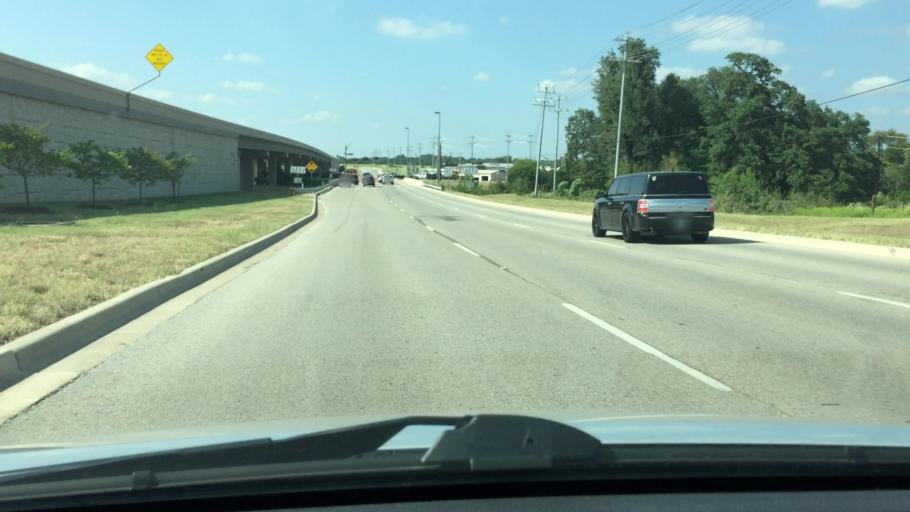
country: US
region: Texas
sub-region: Williamson County
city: Leander
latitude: 30.5807
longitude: -97.8345
